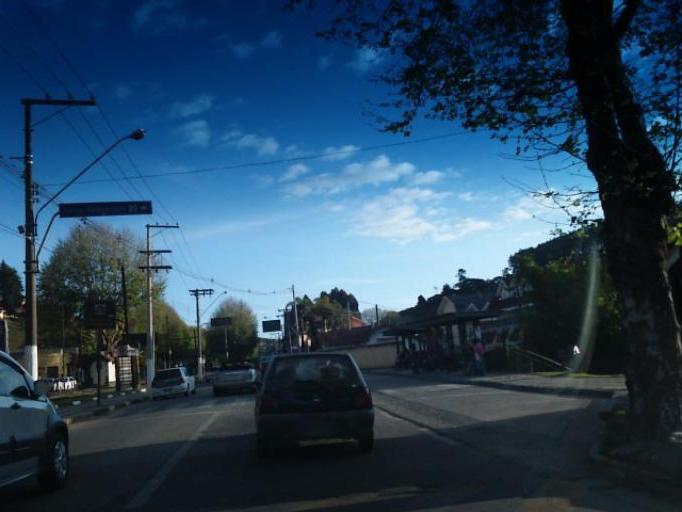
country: BR
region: Sao Paulo
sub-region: Campos Do Jordao
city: Campos do Jordao
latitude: -22.7288
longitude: -45.5822
